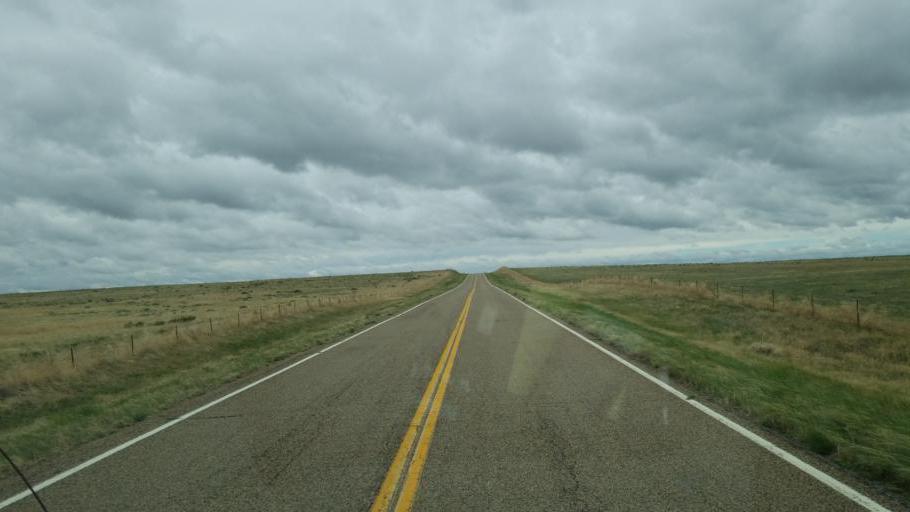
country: US
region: Colorado
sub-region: Lincoln County
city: Hugo
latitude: 38.8508
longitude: -103.5778
